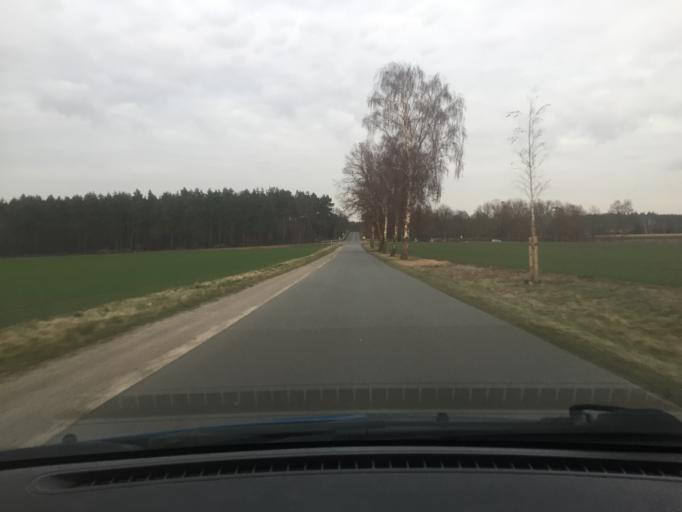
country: DE
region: Lower Saxony
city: Jelmstorf
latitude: 53.1063
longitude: 10.5362
